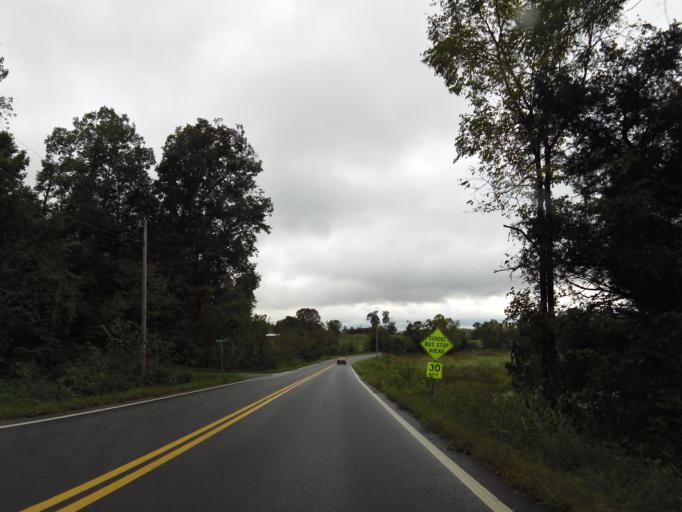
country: US
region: Tennessee
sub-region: Hamilton County
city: Lakesite
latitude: 35.1697
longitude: -85.0146
